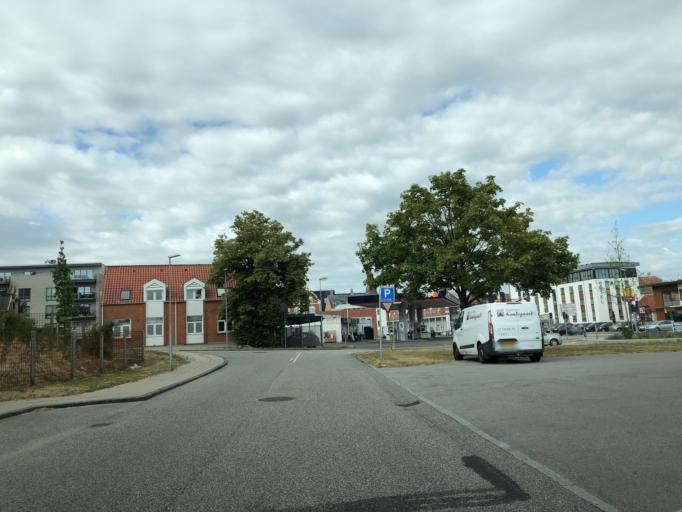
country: DK
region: Central Jutland
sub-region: Skive Kommune
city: Skive
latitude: 56.5639
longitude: 9.0288
